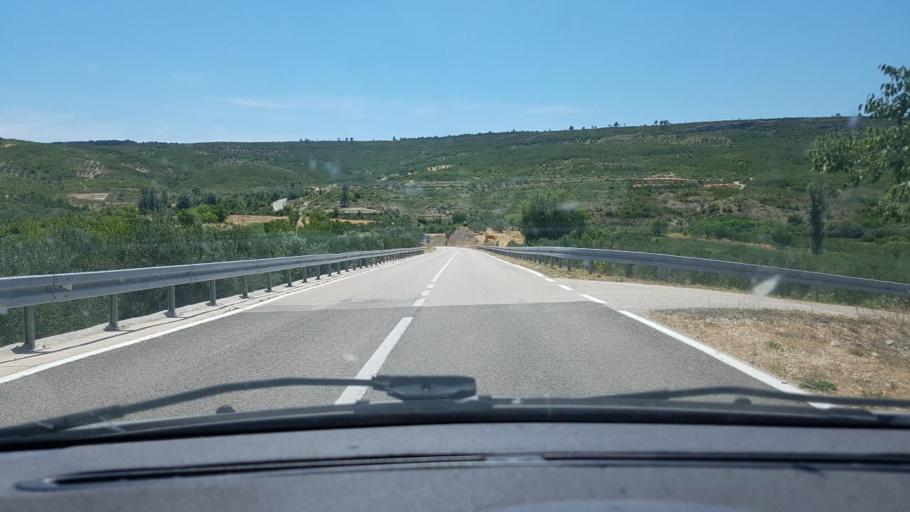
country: HR
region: Sibensko-Kniniska
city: Kistanje
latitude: 43.9100
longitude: 15.9183
